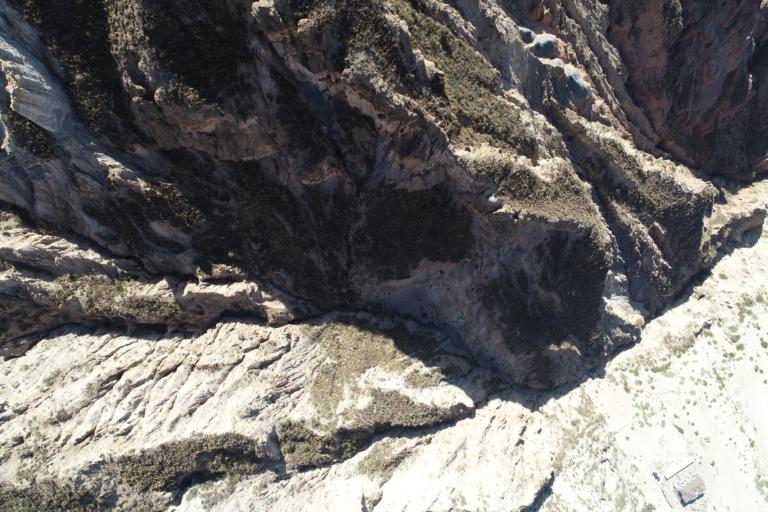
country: BO
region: La Paz
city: La Paz
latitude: -16.5534
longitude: -68.1055
